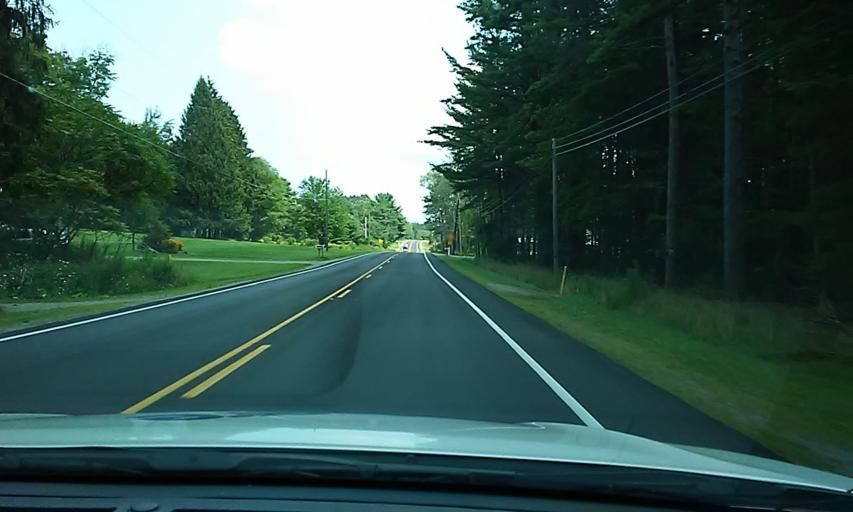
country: US
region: Pennsylvania
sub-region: Elk County
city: Saint Marys
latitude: 41.4483
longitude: -78.4641
